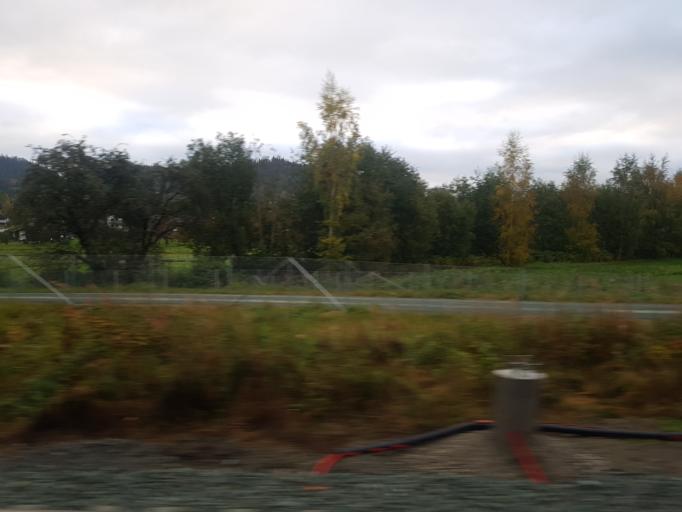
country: NO
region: Sor-Trondelag
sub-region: Melhus
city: Lundamo
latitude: 63.2008
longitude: 10.3030
